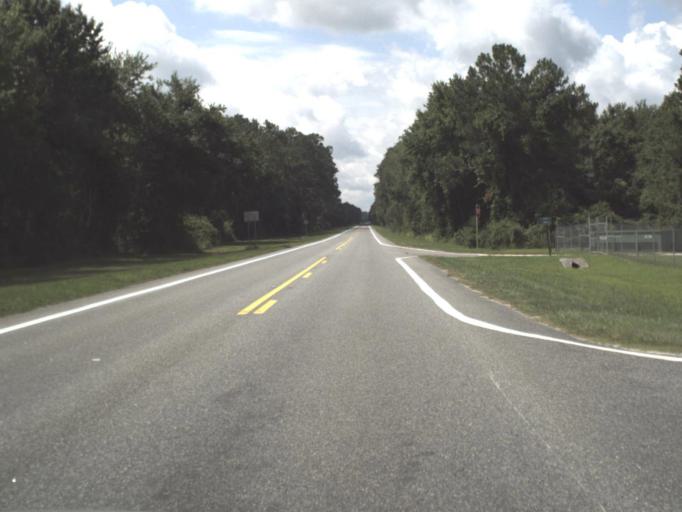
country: US
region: Florida
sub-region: Union County
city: Lake Butler
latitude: 30.0977
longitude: -82.2161
